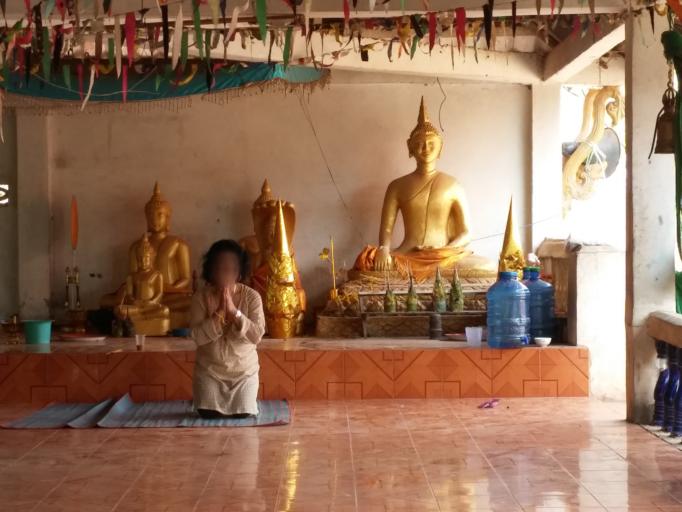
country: LA
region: Champasak
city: Khong
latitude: 14.0991
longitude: 105.7349
